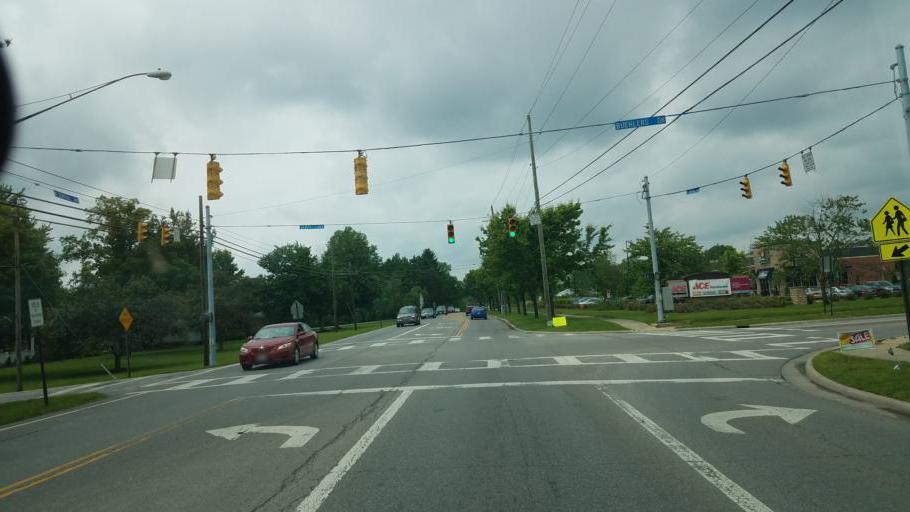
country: US
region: Ohio
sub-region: Delaware County
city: Delaware
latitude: 40.3069
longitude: -83.0938
